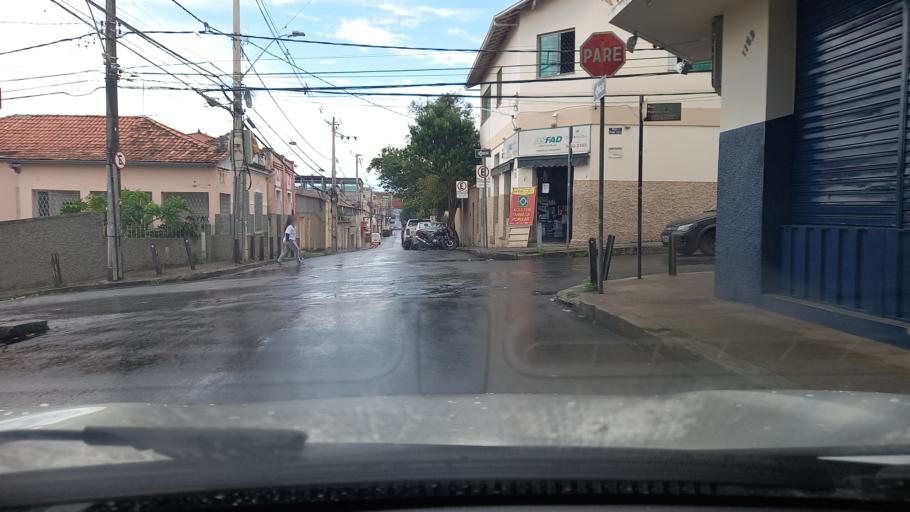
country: BR
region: Minas Gerais
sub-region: Belo Horizonte
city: Belo Horizonte
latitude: -19.9044
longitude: -43.9532
